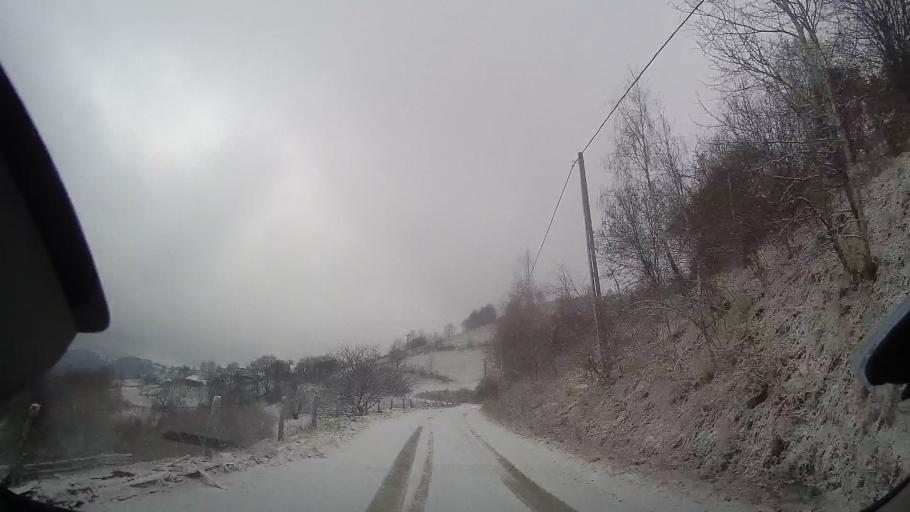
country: RO
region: Cluj
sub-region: Comuna Maguri-Racatau
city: Maguri-Racatau
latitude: 46.6650
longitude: 23.1834
